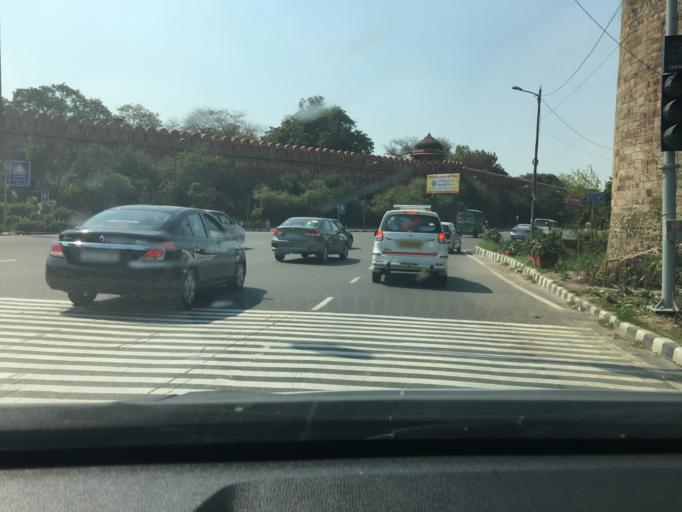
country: IN
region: NCT
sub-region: North Delhi
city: Delhi
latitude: 28.6592
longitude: 77.2443
